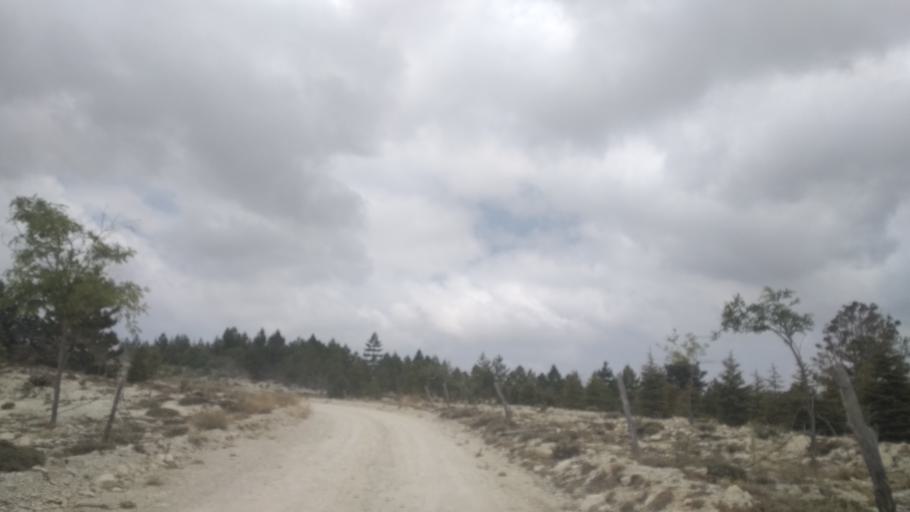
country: TR
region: Mersin
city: Sarikavak
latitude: 36.5740
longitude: 33.7601
